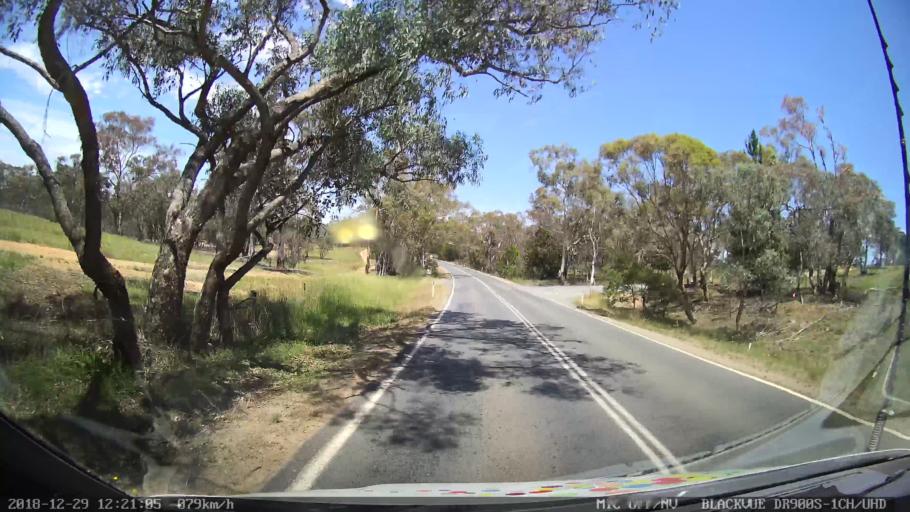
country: AU
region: New South Wales
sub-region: Queanbeyan
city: Queanbeyan
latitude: -35.4097
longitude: 149.2256
